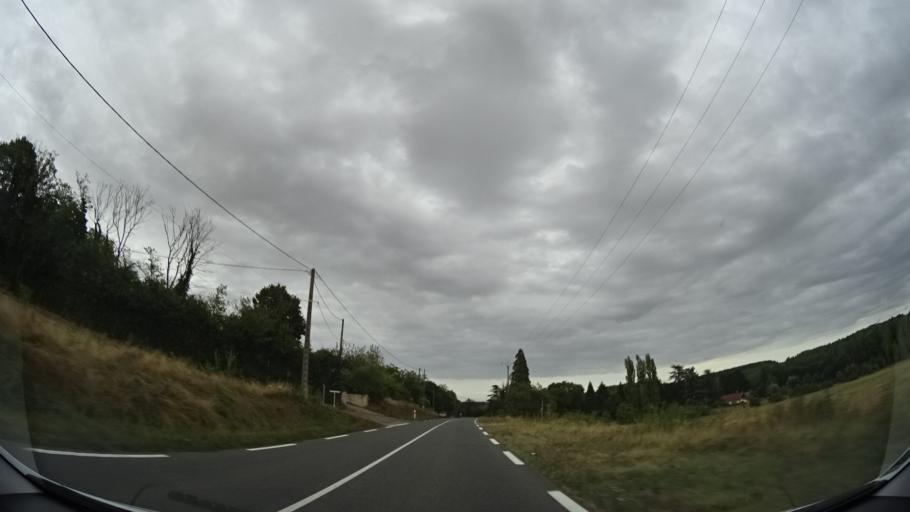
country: FR
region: Centre
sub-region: Departement du Loiret
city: Saint-Germain-des-Pres
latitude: 47.9342
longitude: 2.9011
